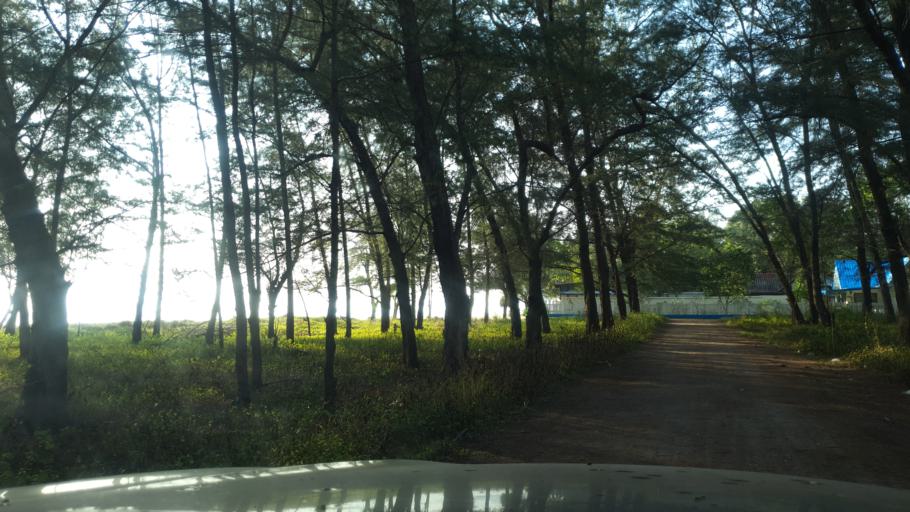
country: TH
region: Prachuap Khiri Khan
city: Bang Saphan
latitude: 11.2824
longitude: 99.5498
